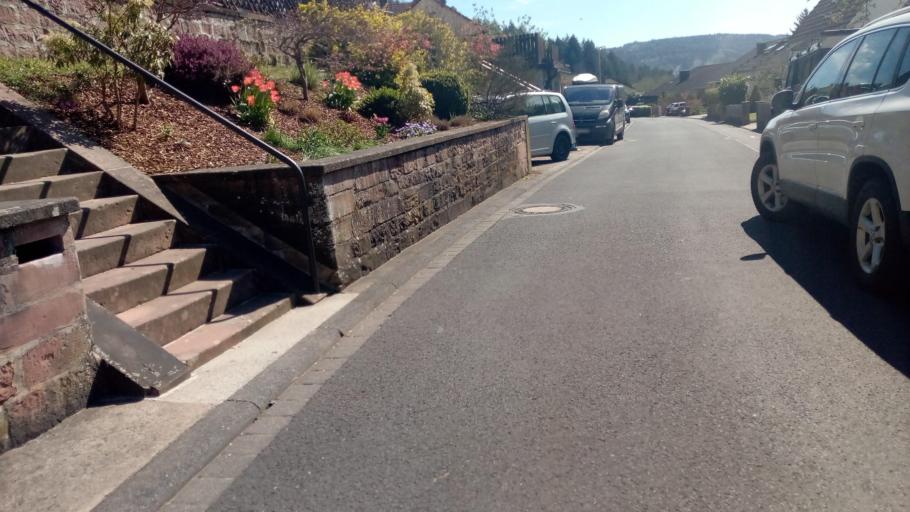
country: DE
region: Bavaria
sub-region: Regierungsbezirk Unterfranken
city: Hasloch
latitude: 49.8016
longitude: 9.4986
